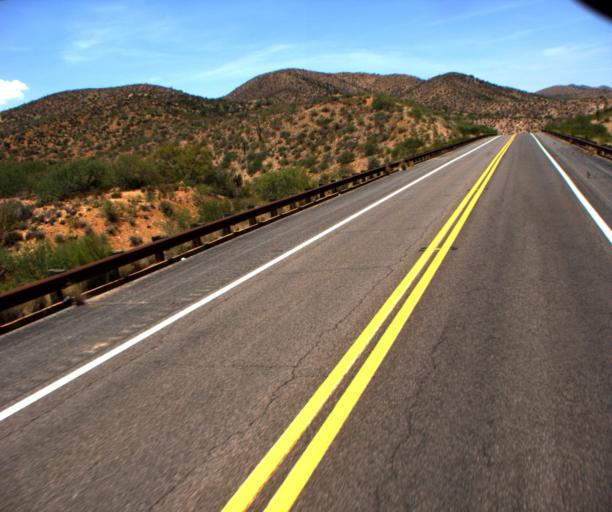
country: US
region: Arizona
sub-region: Gila County
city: Claypool
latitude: 33.4869
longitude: -110.8588
